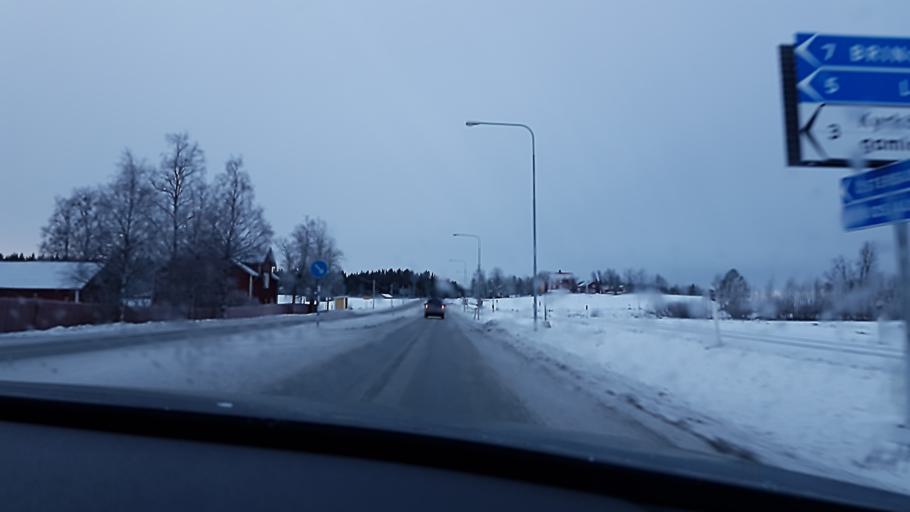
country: SE
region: Jaemtland
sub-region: OEstersunds Kommun
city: Lit
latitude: 63.2387
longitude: 14.7750
